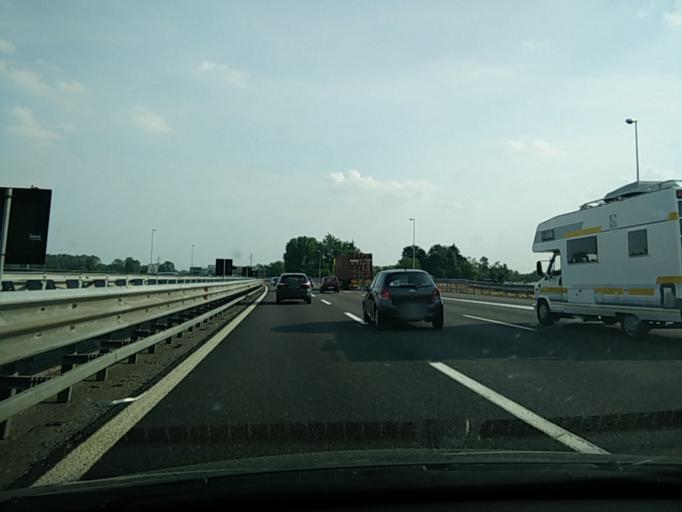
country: IT
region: Lombardy
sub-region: Citta metropolitana di Milano
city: Cesano Boscone
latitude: 45.4440
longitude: 9.0738
